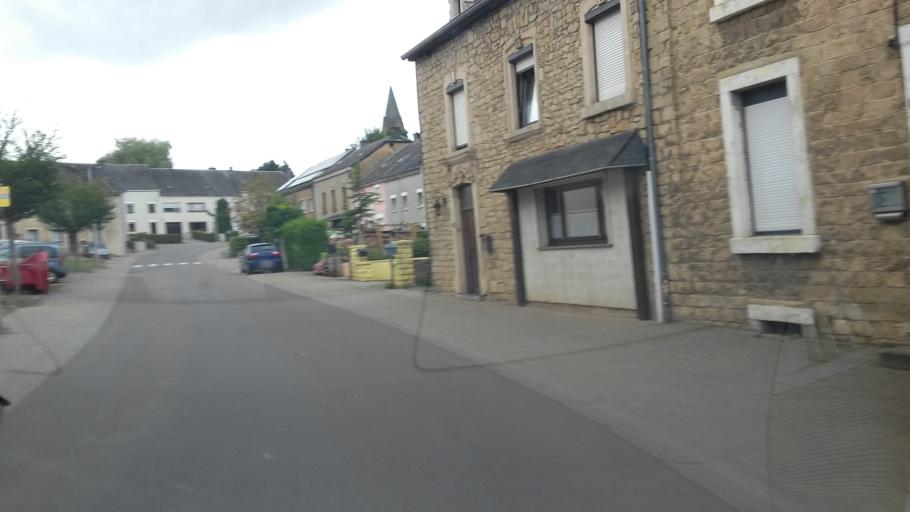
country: BE
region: Wallonia
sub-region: Province du Luxembourg
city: Arlon
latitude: 49.6812
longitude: 5.8394
